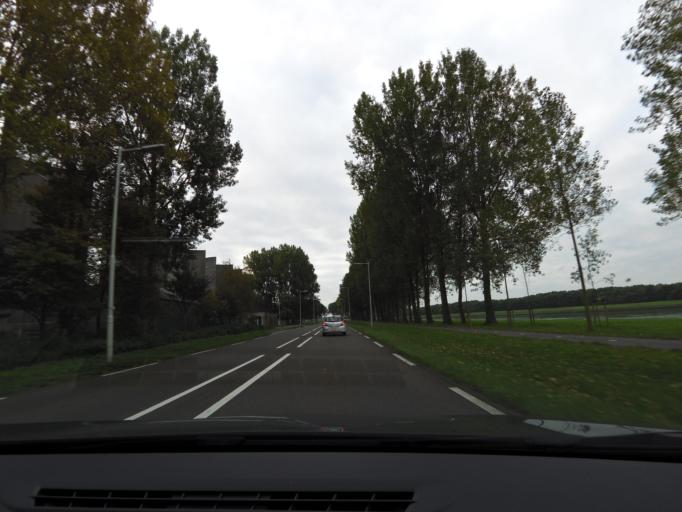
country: NL
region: South Holland
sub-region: Gemeente Maassluis
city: Maassluis
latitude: 51.8960
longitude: 4.2263
